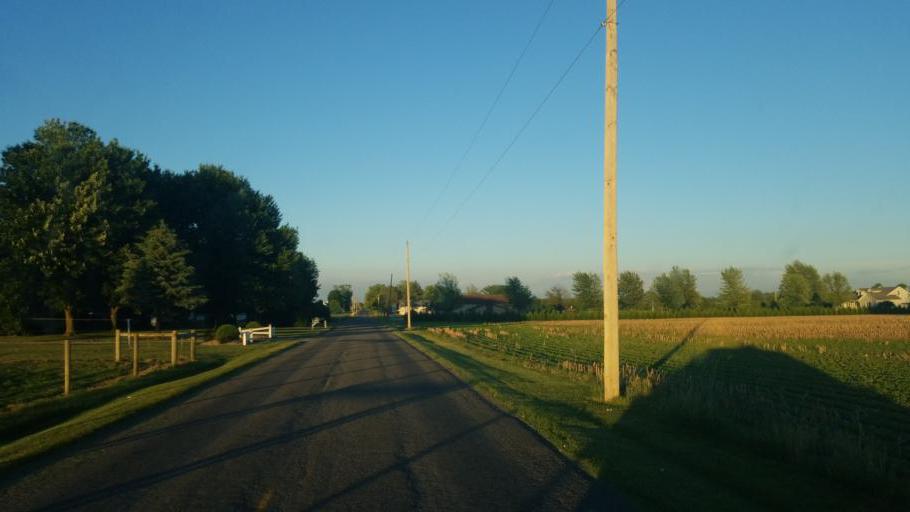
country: US
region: Indiana
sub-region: Elkhart County
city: Nappanee
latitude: 41.4572
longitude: -86.0347
